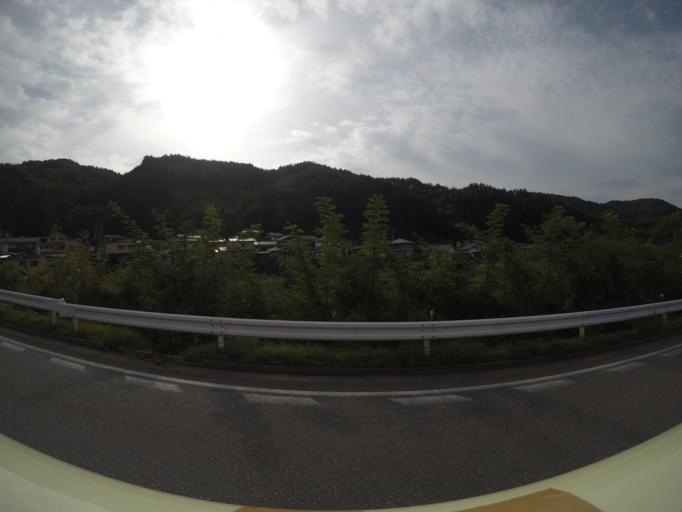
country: JP
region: Nagano
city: Ina
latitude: 35.8614
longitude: 137.7227
